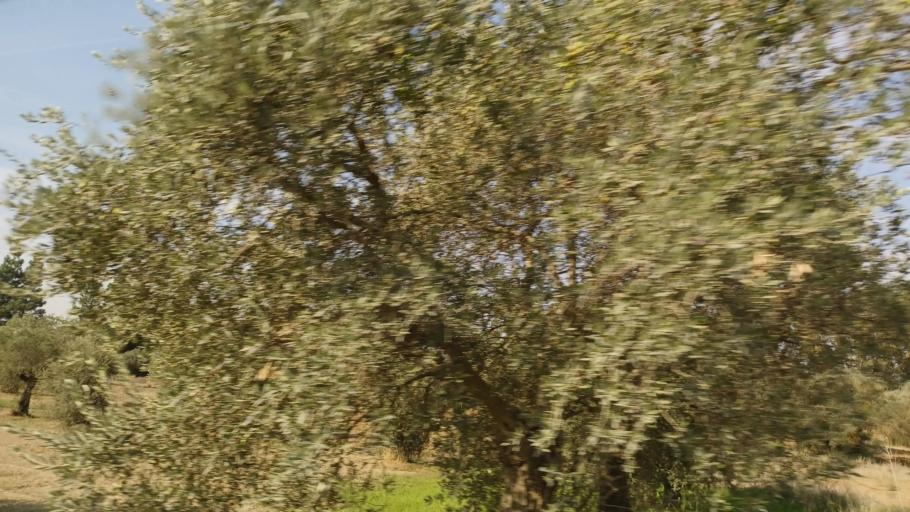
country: CY
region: Larnaka
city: Mosfiloti
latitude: 34.9667
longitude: 33.4135
